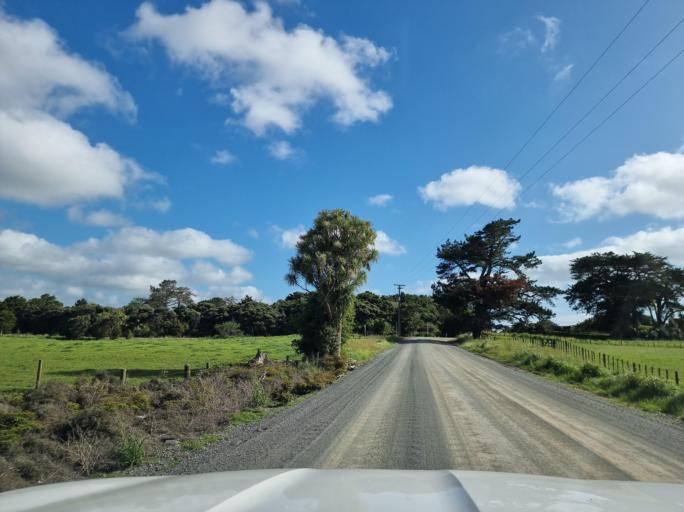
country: NZ
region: Auckland
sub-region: Auckland
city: Wellsford
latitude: -36.1280
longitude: 174.5938
